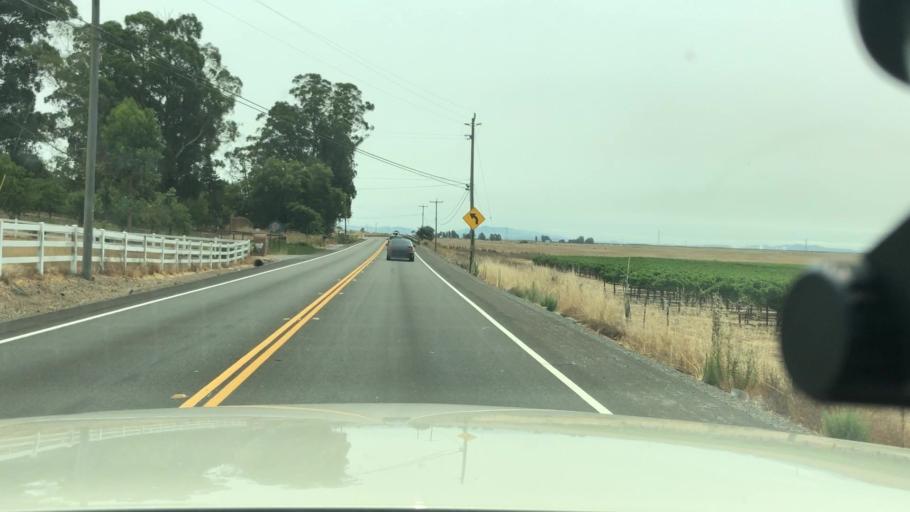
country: US
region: California
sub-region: Marin County
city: Black Point-Green Point
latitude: 38.1554
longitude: -122.4958
